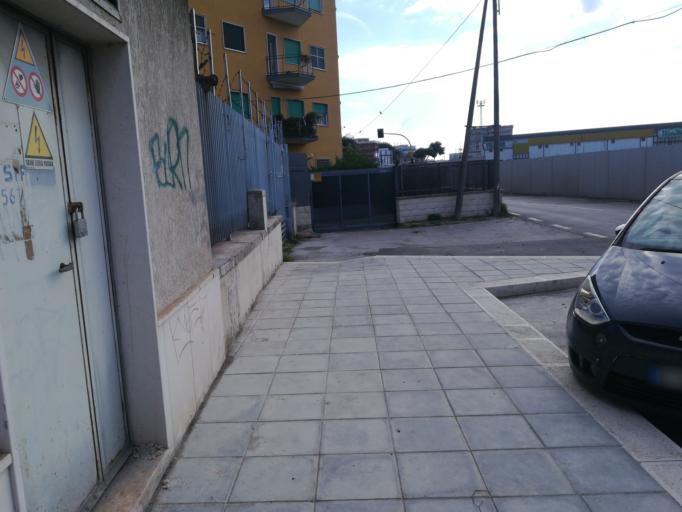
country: IT
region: Apulia
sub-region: Provincia di Bari
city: Bari
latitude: 41.1141
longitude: 16.8860
